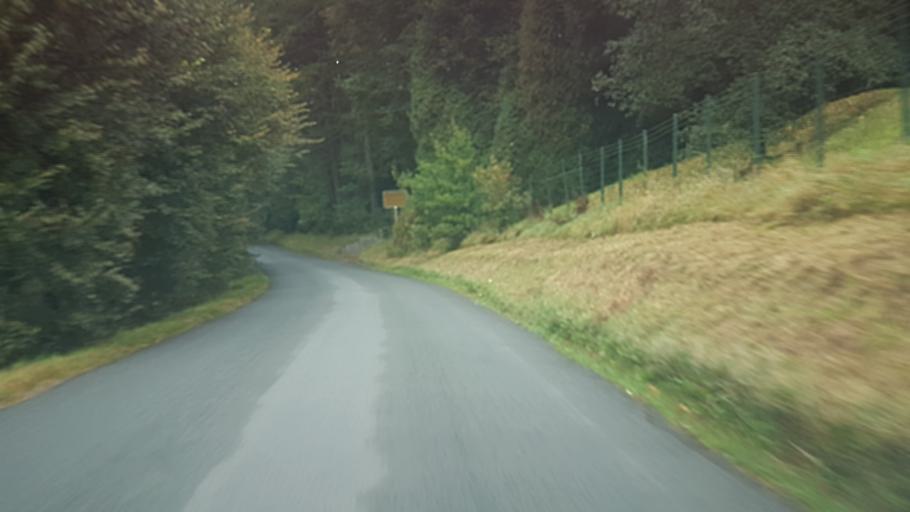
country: DE
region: North Rhine-Westphalia
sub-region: Regierungsbezirk Arnsberg
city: Luedenscheid
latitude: 51.2176
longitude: 7.6900
